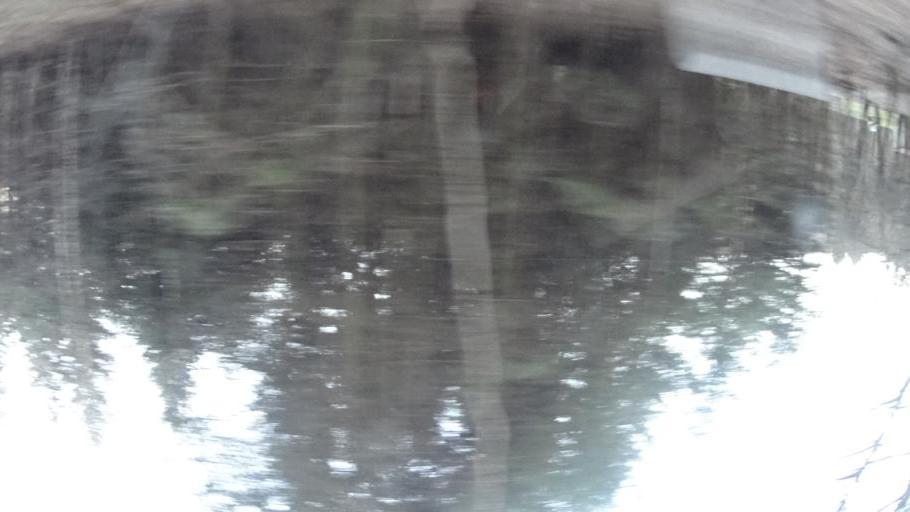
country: DE
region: Bavaria
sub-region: Regierungsbezirk Unterfranken
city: Mombris
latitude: 50.0897
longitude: 9.1695
